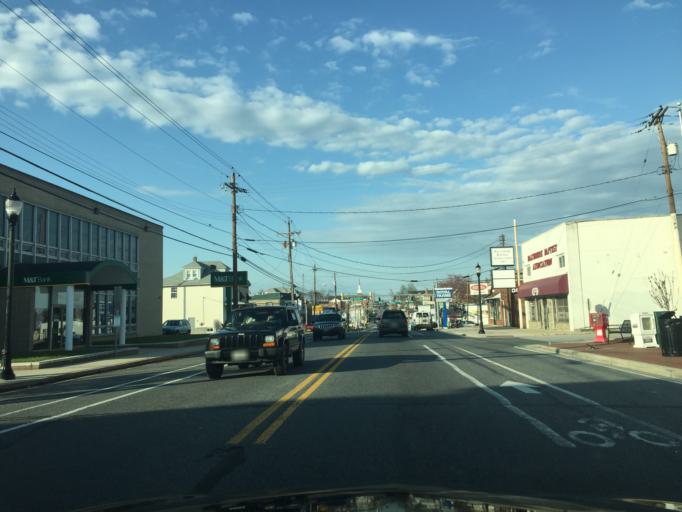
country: US
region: Maryland
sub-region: Baltimore County
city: Parkville
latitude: 39.3781
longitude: -76.5392
